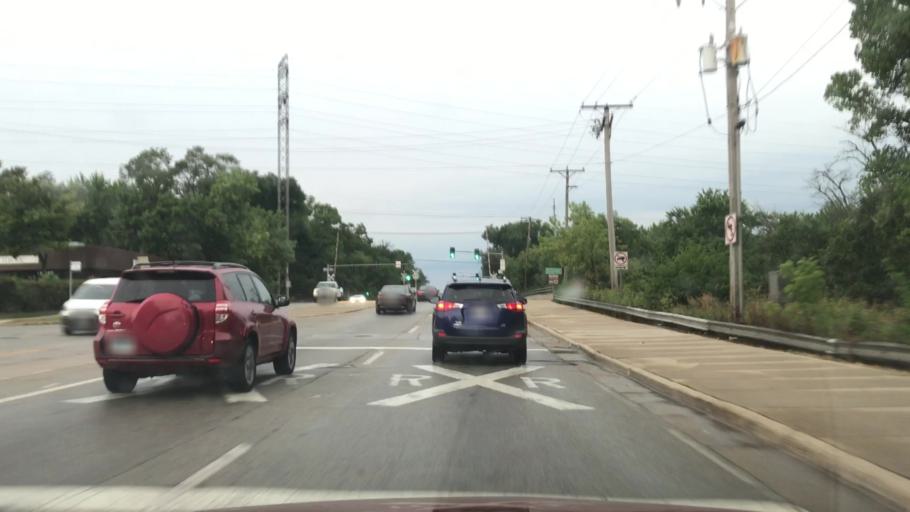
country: US
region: Illinois
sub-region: Cook County
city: Morton Grove
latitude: 42.0410
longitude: -87.7867
